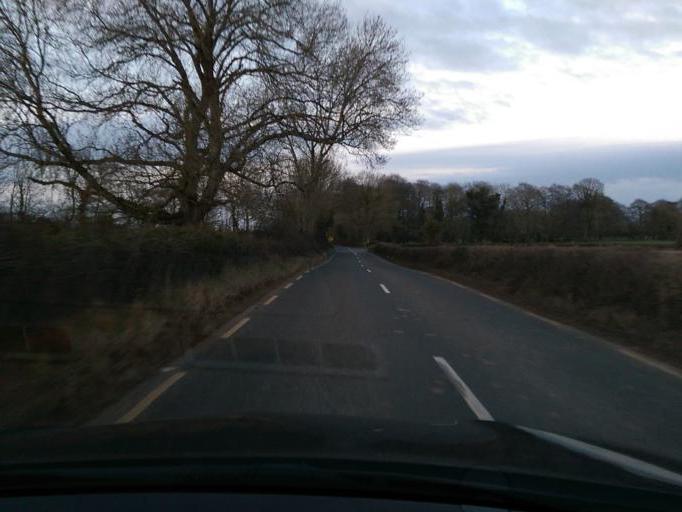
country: IE
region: Leinster
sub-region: Uibh Fhaili
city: Banagher
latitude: 53.0840
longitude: -8.0600
